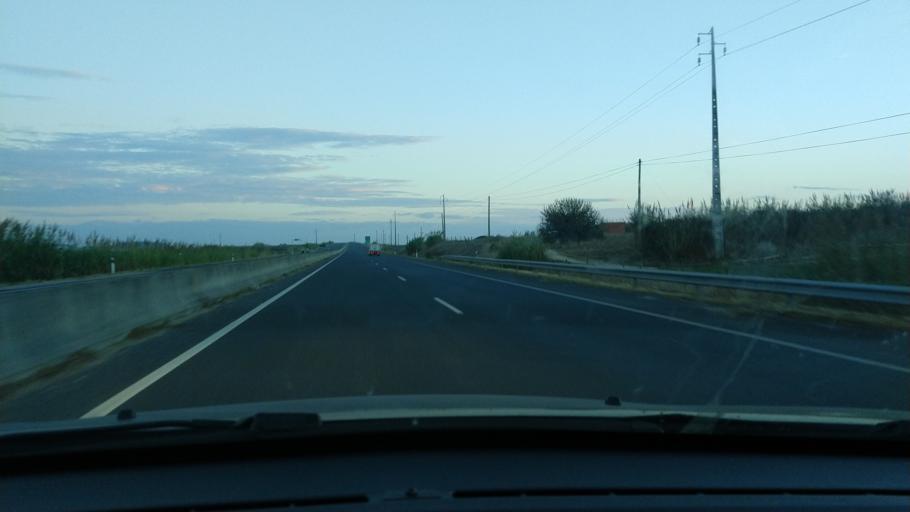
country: PT
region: Leiria
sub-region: Peniche
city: Atouguia da Baleia
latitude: 39.3397
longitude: -9.3382
